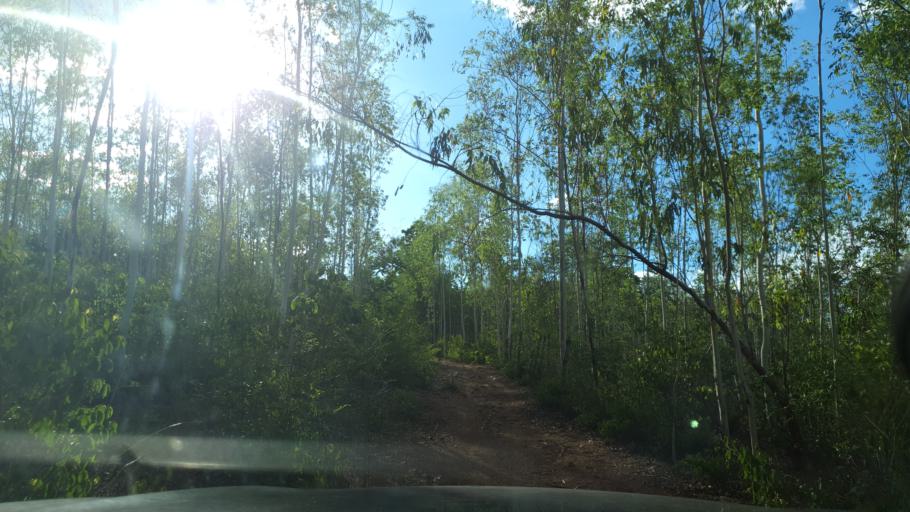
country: TH
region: Lampang
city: Sop Prap
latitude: 17.8929
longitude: 99.2846
